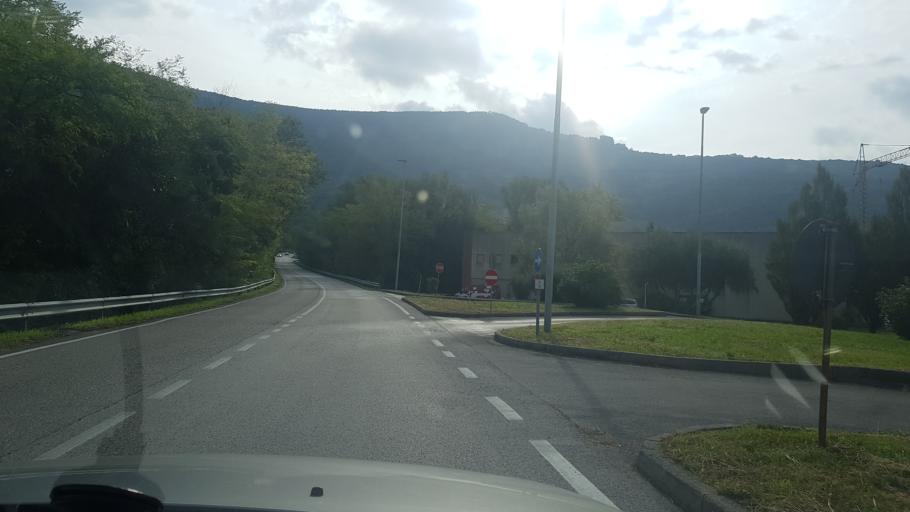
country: IT
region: Friuli Venezia Giulia
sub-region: Provincia di Trieste
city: Dolina
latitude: 45.6050
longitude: 13.8513
